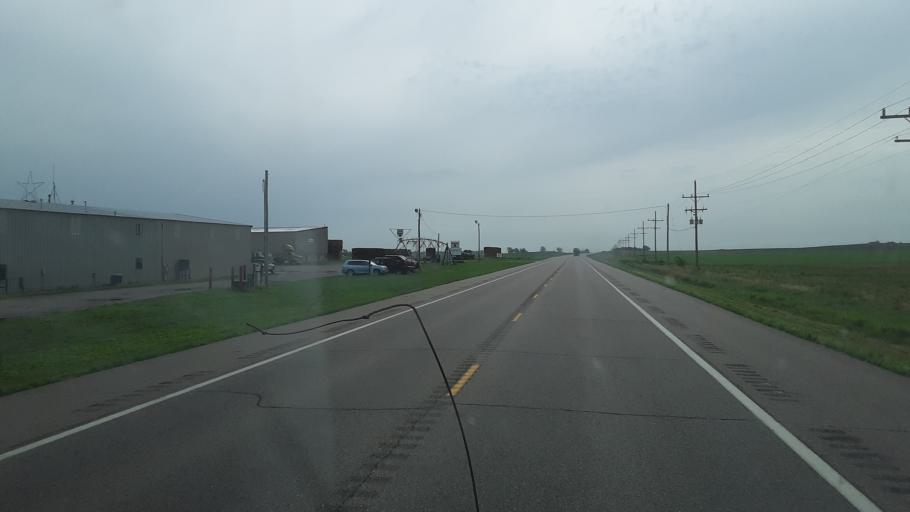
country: US
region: Kansas
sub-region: Edwards County
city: Kinsley
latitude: 37.9275
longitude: -99.2954
